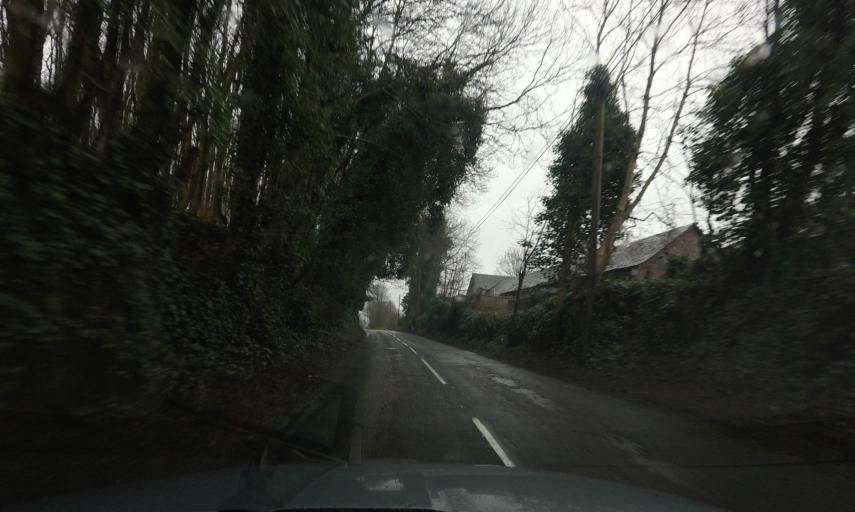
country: GB
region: Scotland
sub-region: Stirling
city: Balfron
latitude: 56.1537
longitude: -4.3623
